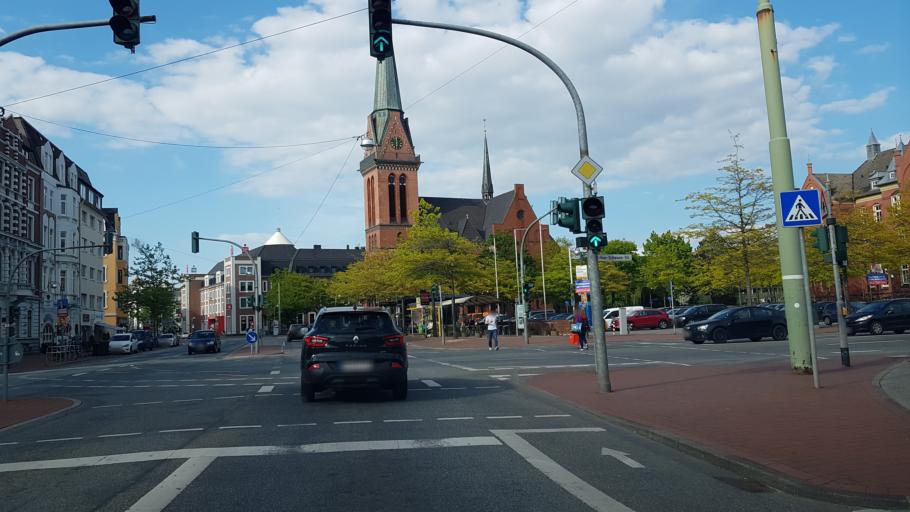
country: DE
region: Bremen
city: Bremerhaven
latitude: 53.5573
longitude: 8.5850
